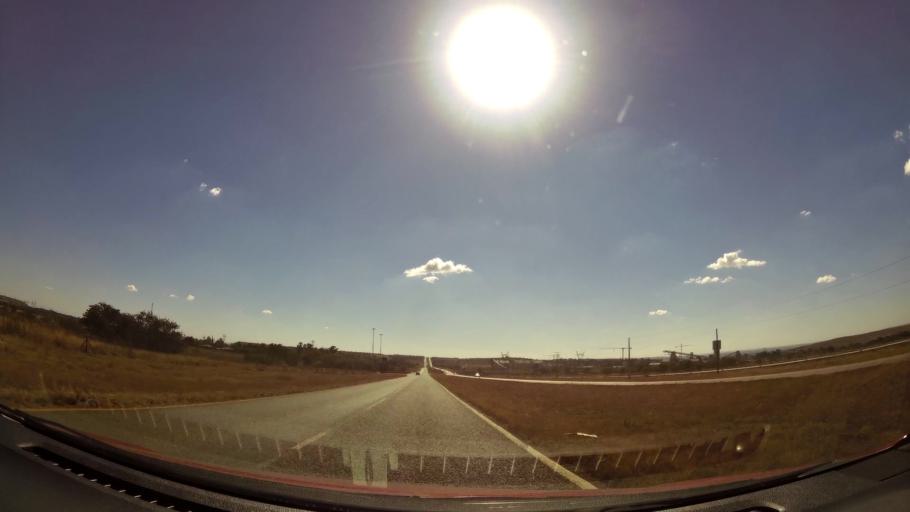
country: ZA
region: Gauteng
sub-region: West Rand District Municipality
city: Carletonville
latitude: -26.4093
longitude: 27.4301
